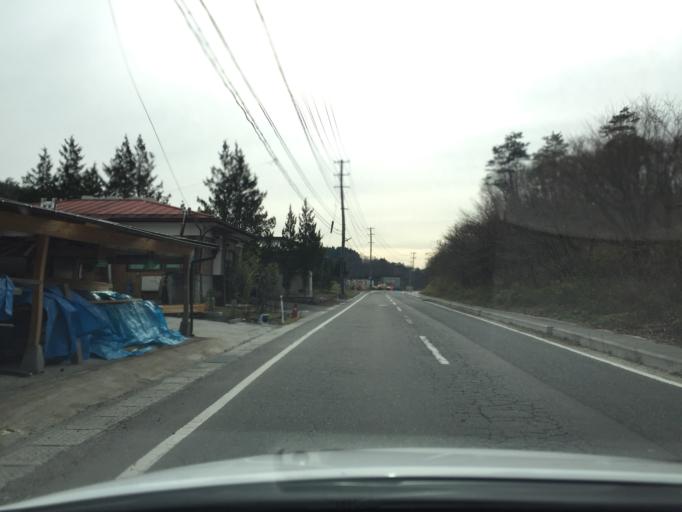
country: JP
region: Fukushima
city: Ishikawa
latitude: 37.2277
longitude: 140.5676
